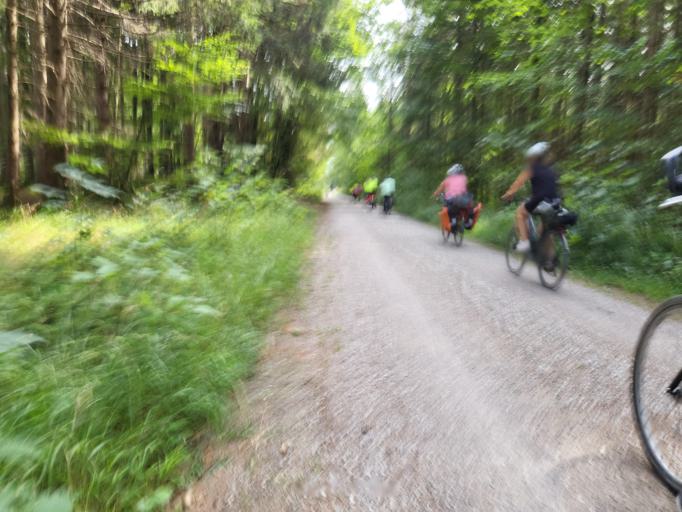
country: DE
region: Bavaria
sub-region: Upper Bavaria
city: Hohenkirchen-Siegertsbrunn
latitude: 48.0129
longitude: 11.7532
